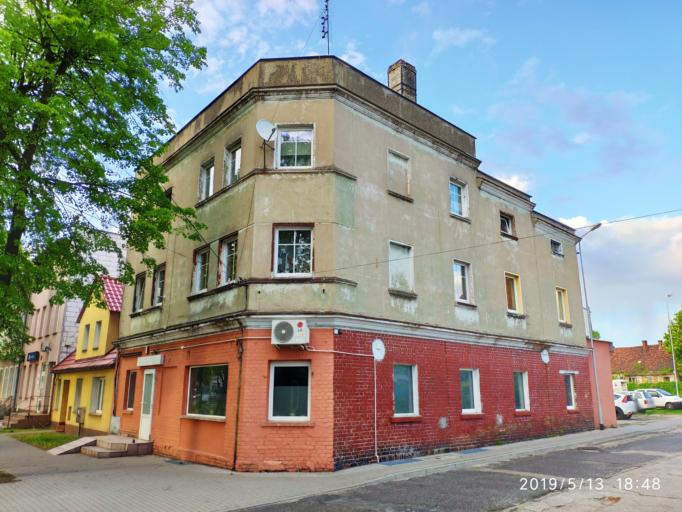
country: PL
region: Lubusz
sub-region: Powiat zielonogorski
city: Czerwiensk
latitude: 52.0123
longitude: 15.4217
